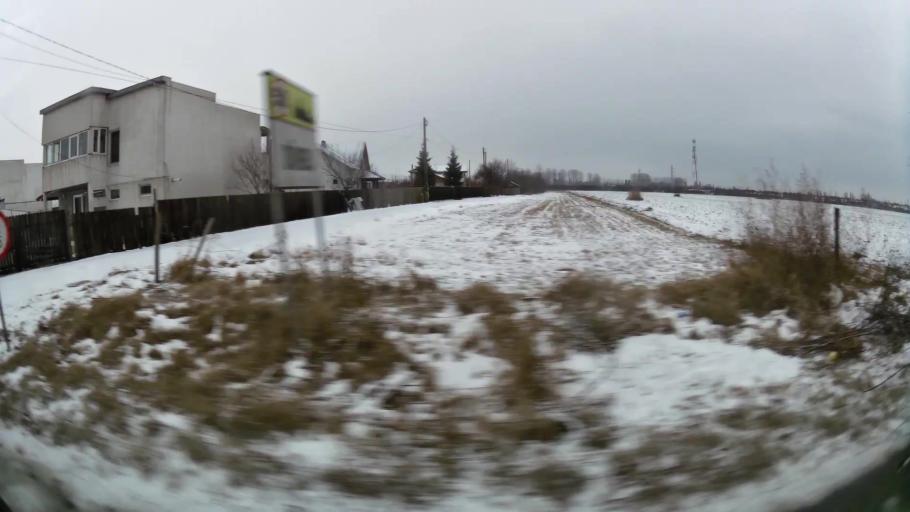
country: RO
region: Prahova
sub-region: Comuna Berceni
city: Corlatesti
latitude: 44.9272
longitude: 26.0685
